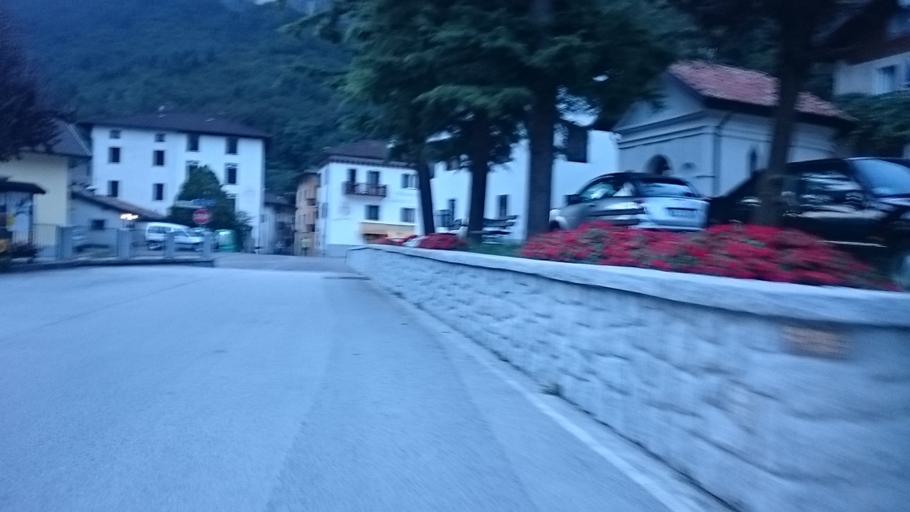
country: IT
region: Trentino-Alto Adige
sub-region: Provincia di Trento
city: Grigno
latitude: 46.0168
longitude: 11.6364
